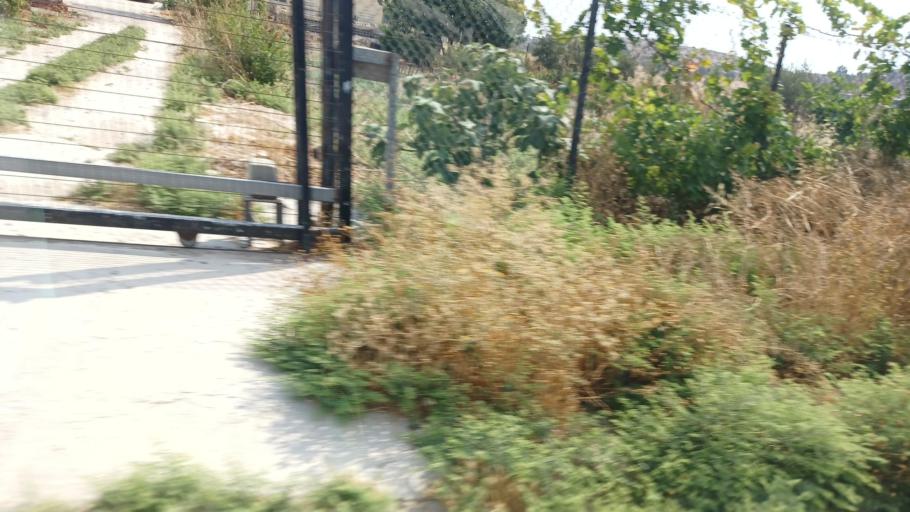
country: CY
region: Larnaka
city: Aradippou
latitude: 34.9192
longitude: 33.5379
